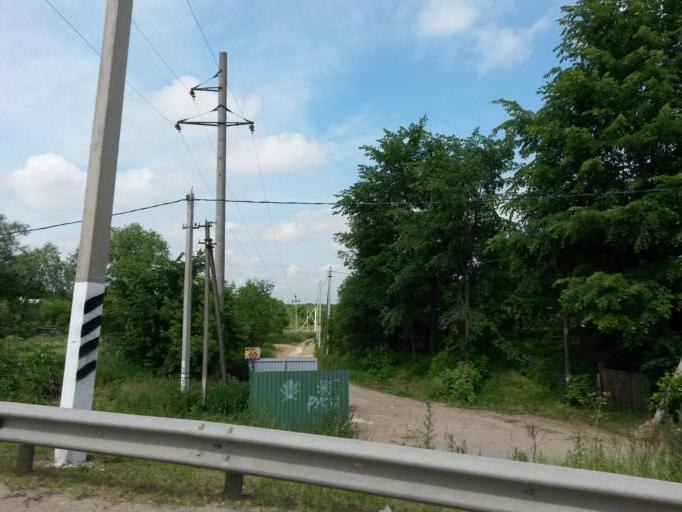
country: RU
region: Moskovskaya
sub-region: Chekhovskiy Rayon
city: Chekhov
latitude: 55.1817
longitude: 37.4909
